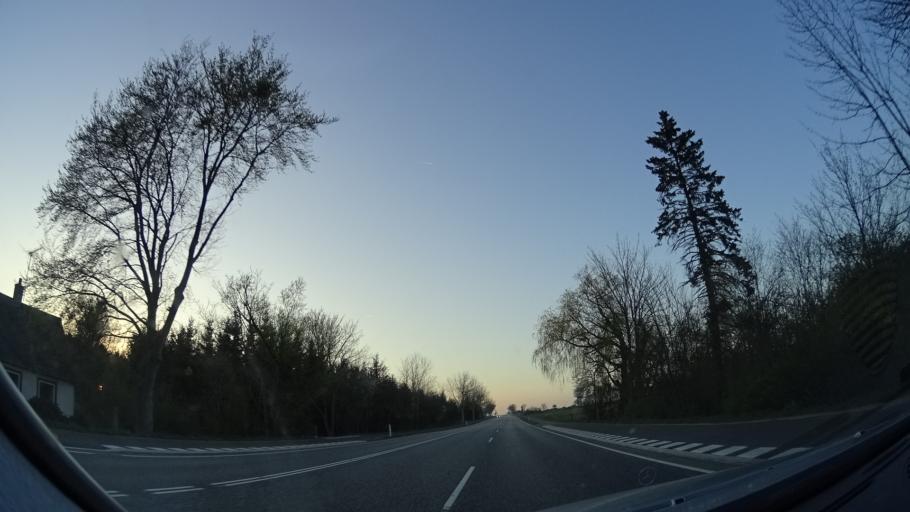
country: DK
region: Zealand
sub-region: Solrod Kommune
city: Havdrup
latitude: 55.5801
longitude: 12.1105
